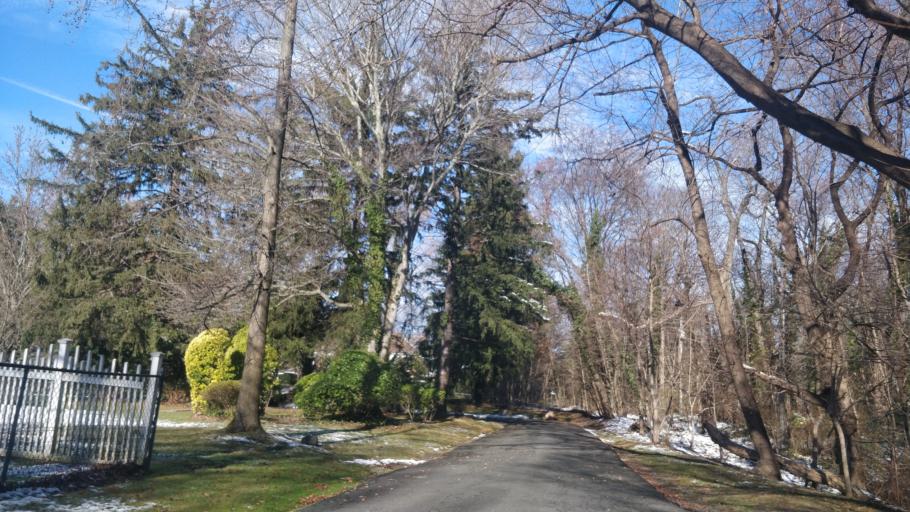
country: US
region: New York
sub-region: Nassau County
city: Locust Valley
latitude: 40.8793
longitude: -73.6103
